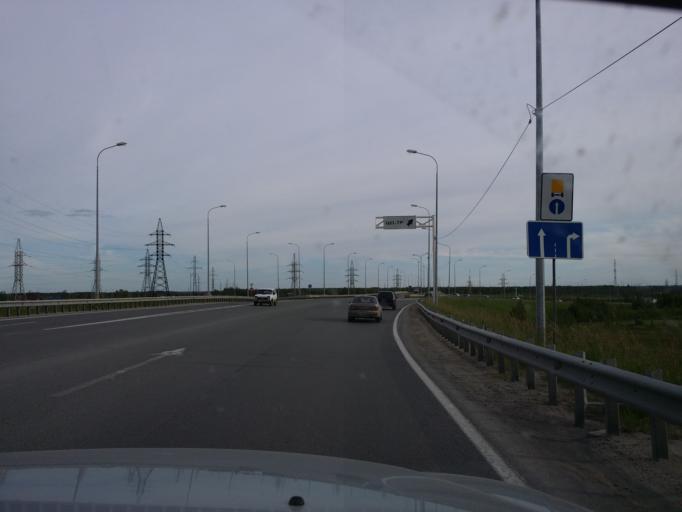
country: RU
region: Khanty-Mansiyskiy Avtonomnyy Okrug
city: Nizhnevartovsk
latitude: 60.9504
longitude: 76.6635
